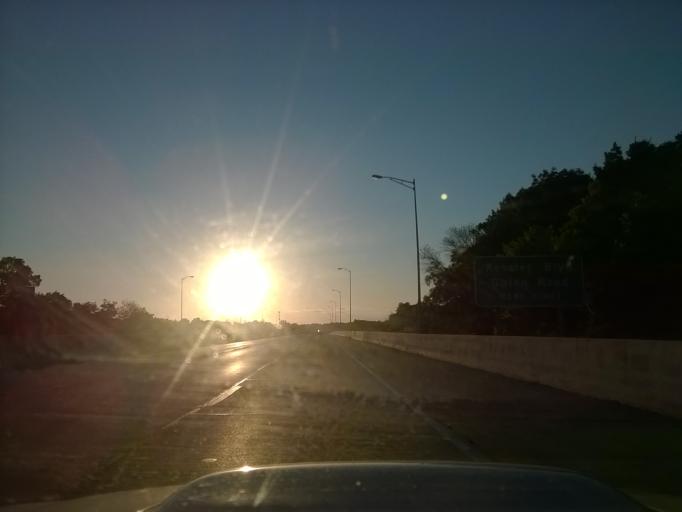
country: US
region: Indiana
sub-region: Marion County
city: Indianapolis
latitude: 39.8172
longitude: -86.1878
